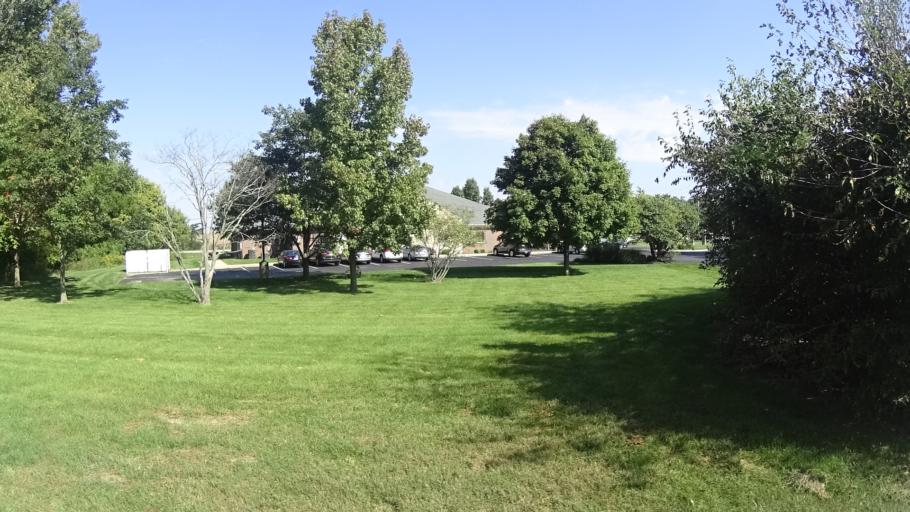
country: US
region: Indiana
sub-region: Madison County
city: Lapel
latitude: 40.0758
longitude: -85.8493
